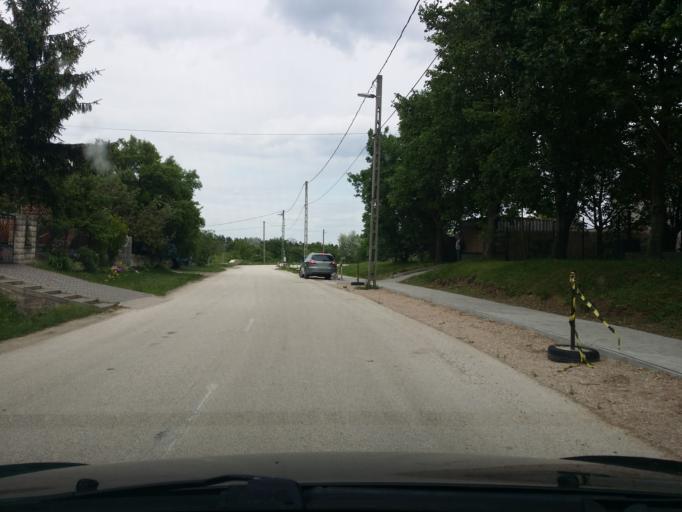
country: HU
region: Veszprem
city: Szentkiralyszabadja
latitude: 47.0596
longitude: 17.9731
